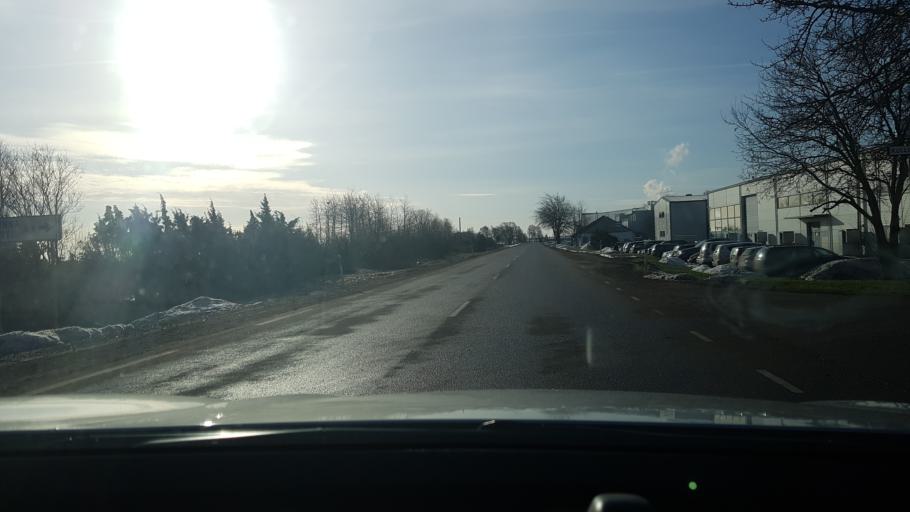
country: EE
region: Saare
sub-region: Kuressaare linn
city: Kuressaare
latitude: 58.2242
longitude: 22.5062
